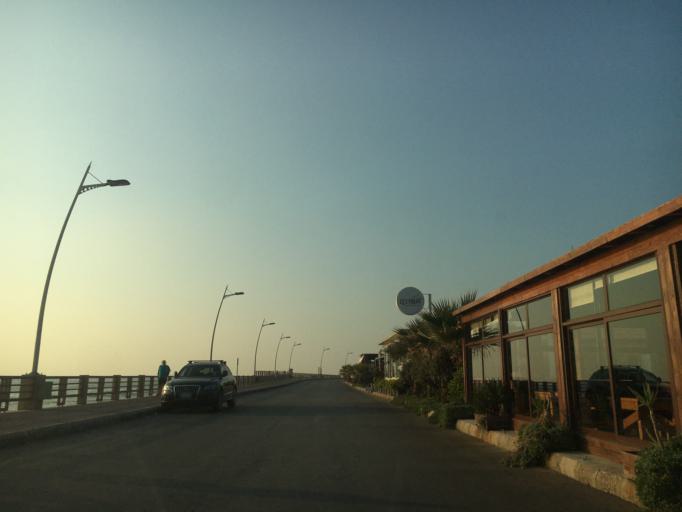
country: LB
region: Mont-Liban
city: Jbail
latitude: 34.1430
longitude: 35.6282
